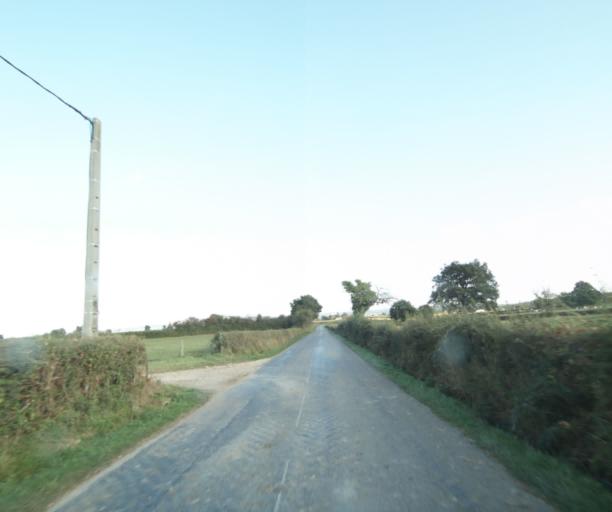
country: FR
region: Bourgogne
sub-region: Departement de Saone-et-Loire
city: Palinges
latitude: 46.5648
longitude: 4.1796
